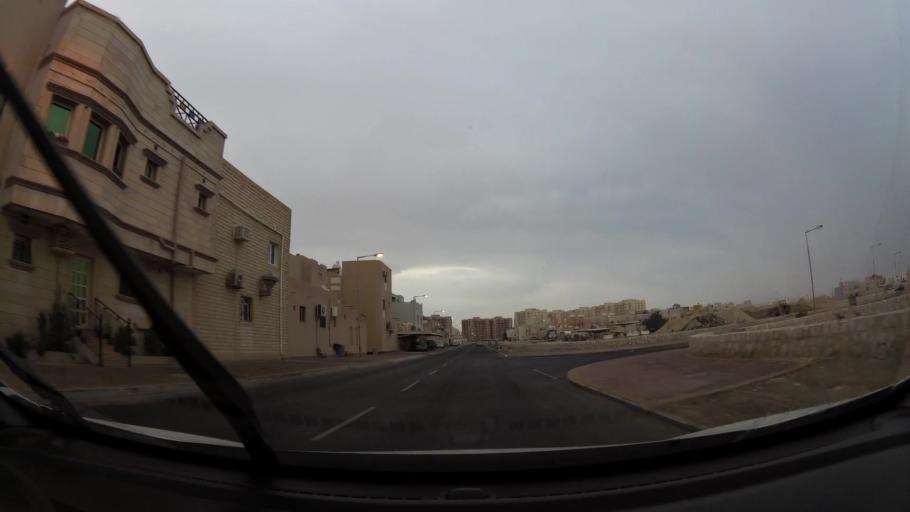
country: BH
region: Central Governorate
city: Madinat Hamad
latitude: 26.1261
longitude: 50.4883
